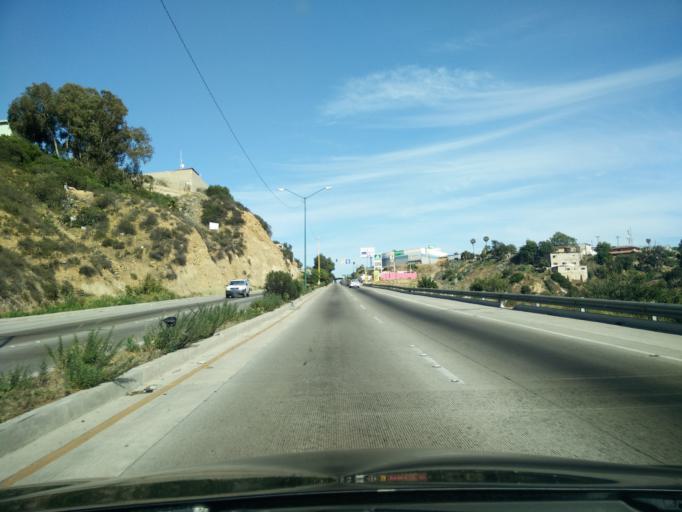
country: US
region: California
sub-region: San Diego County
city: Imperial Beach
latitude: 32.5315
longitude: -117.0797
